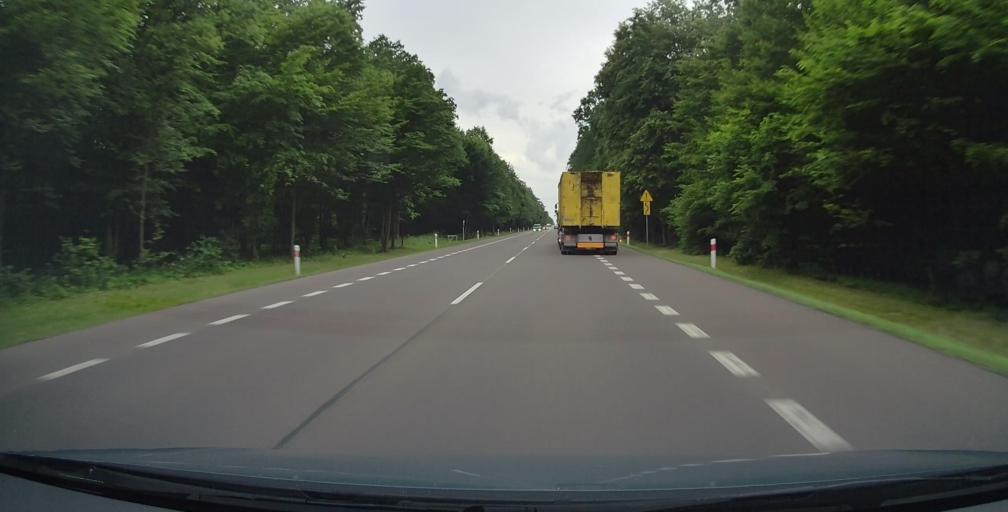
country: PL
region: Lublin Voivodeship
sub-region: Powiat bialski
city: Zalesie
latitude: 52.0366
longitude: 23.4334
